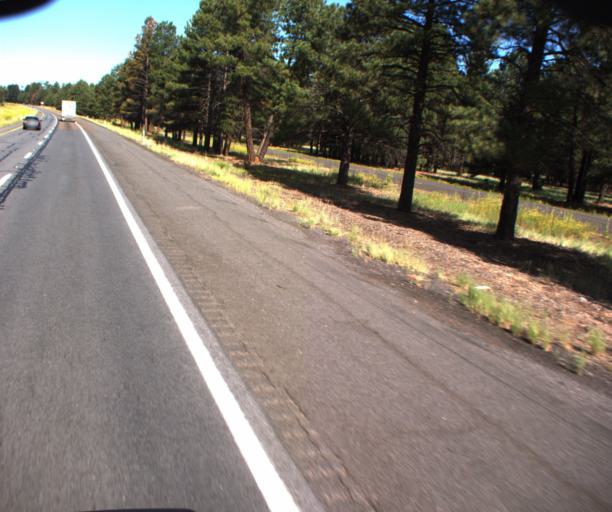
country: US
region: Arizona
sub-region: Coconino County
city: Parks
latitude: 35.2480
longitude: -111.8494
